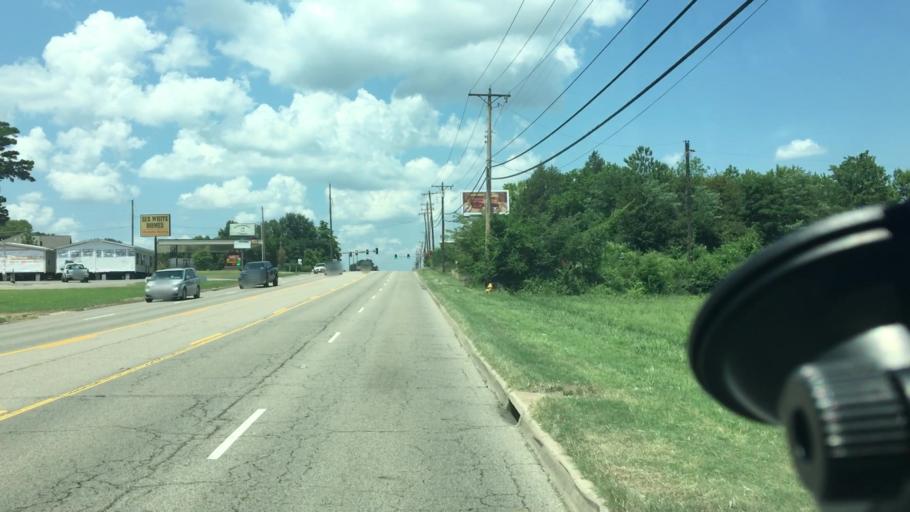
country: US
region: Arkansas
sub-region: Sebastian County
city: Barling
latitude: 35.3445
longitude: -94.3292
